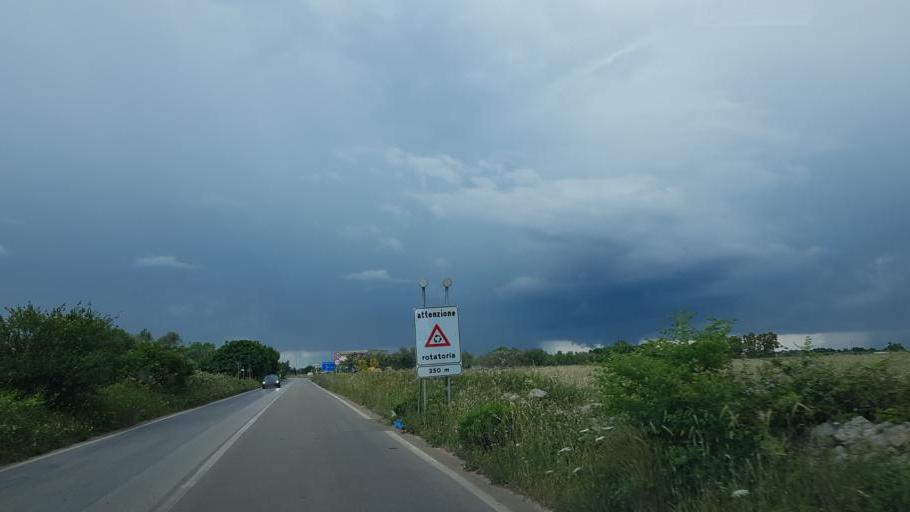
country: IT
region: Apulia
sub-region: Provincia di Lecce
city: Porto Cesareo
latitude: 40.2999
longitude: 17.8581
